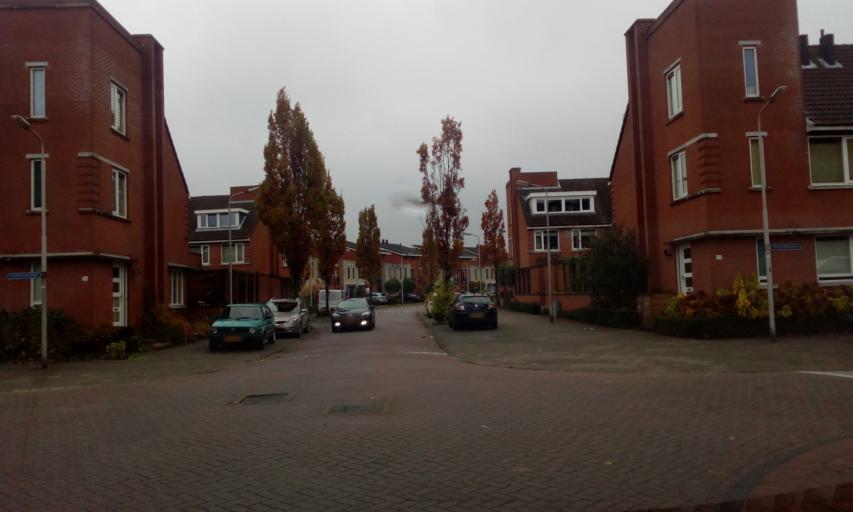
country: NL
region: South Holland
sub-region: Gemeente Lansingerland
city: Berkel en Rodenrijs
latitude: 51.9847
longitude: 4.4676
